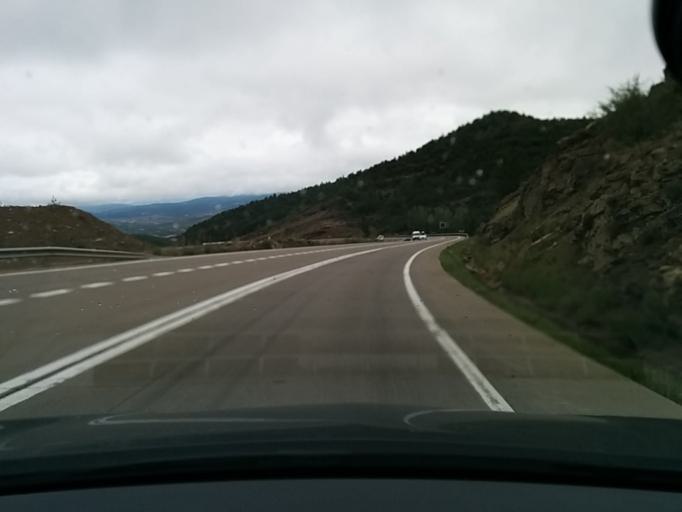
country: ES
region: Aragon
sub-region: Provincia de Huesca
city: Arguis
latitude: 42.3797
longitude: -0.3731
